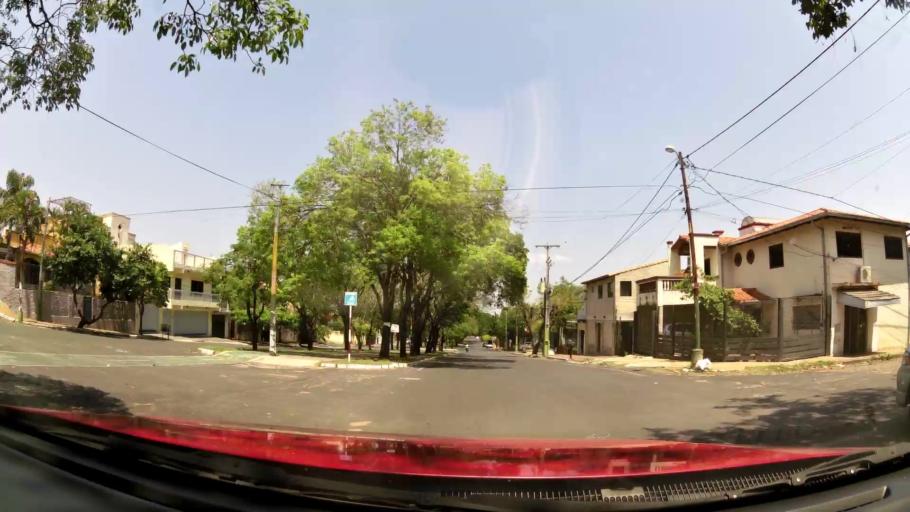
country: PY
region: Asuncion
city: Asuncion
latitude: -25.3008
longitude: -57.6450
